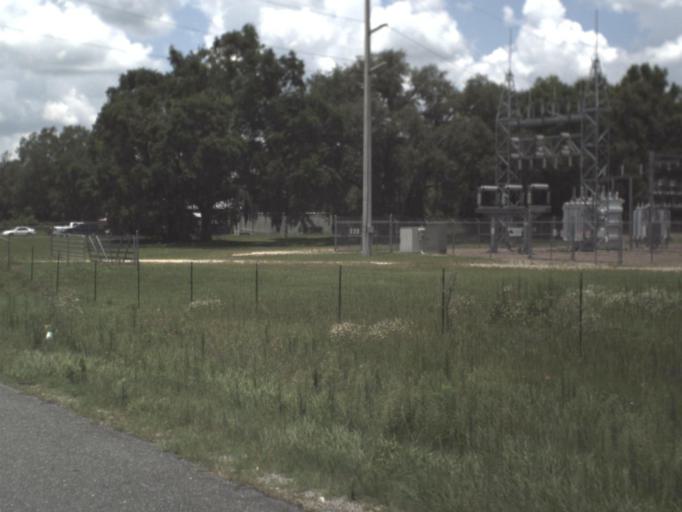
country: US
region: Florida
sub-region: Alachua County
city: Newberry
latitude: 29.6356
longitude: -82.6867
